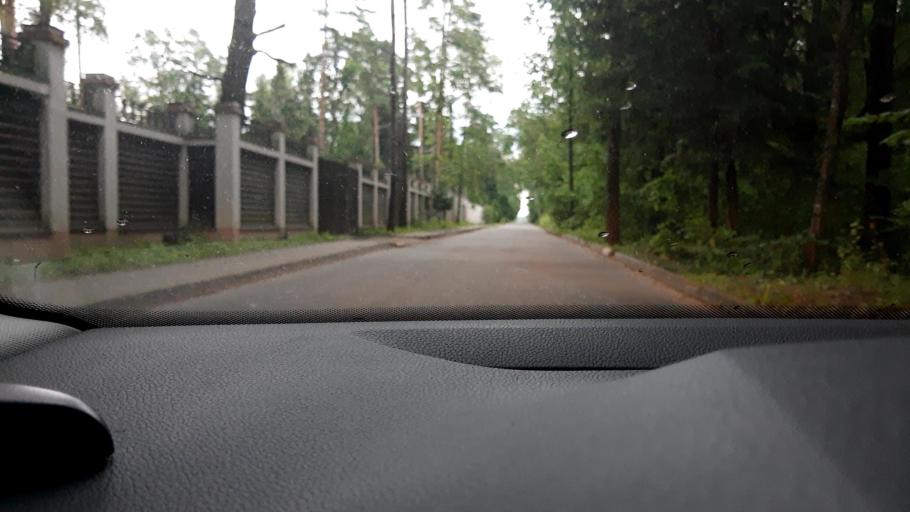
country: RU
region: Moskovskaya
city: Novopodrezkovo
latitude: 55.8929
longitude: 37.3365
